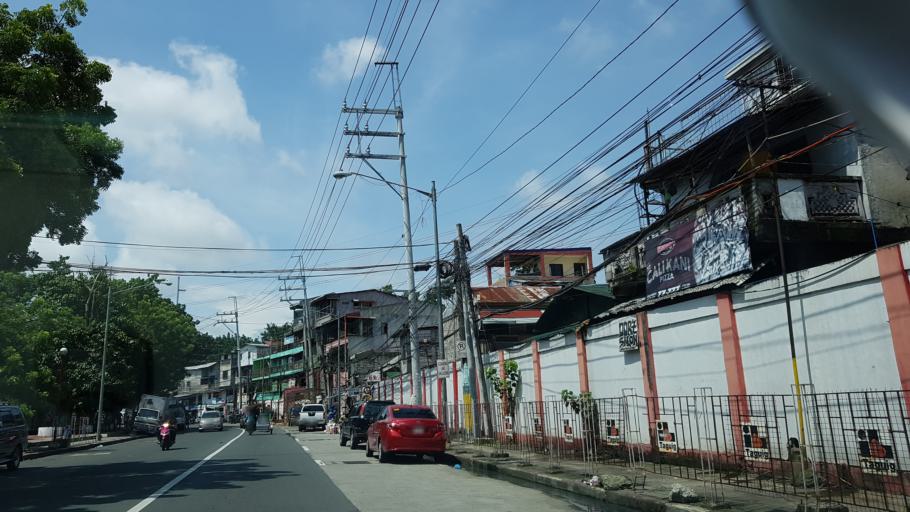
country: PH
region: Metro Manila
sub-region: Makati City
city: Makati City
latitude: 14.5278
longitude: 121.0265
